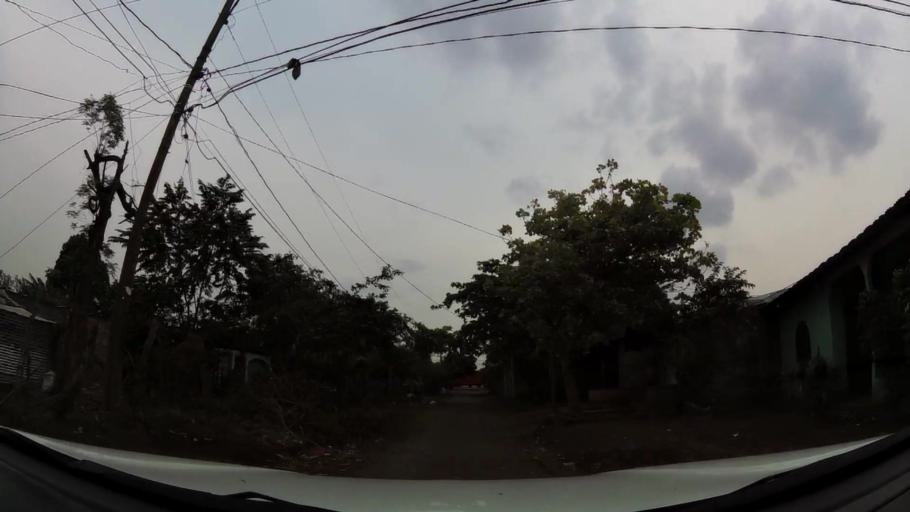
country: NI
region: Leon
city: Leon
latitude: 12.4521
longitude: -86.8648
